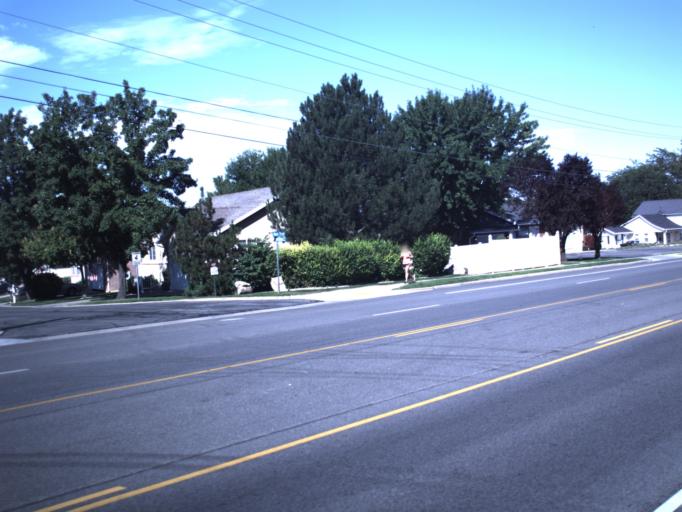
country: US
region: Utah
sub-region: Davis County
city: Kaysville
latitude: 41.0309
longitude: -111.9356
